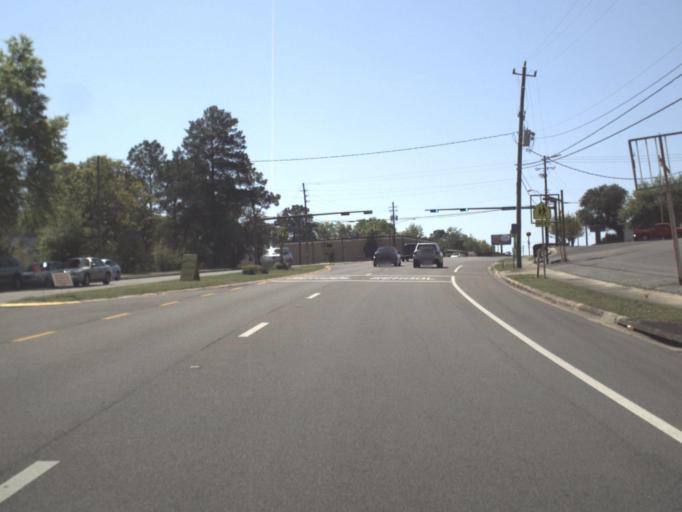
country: US
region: Florida
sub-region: Okaloosa County
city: Valparaiso
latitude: 30.5140
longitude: -86.4943
